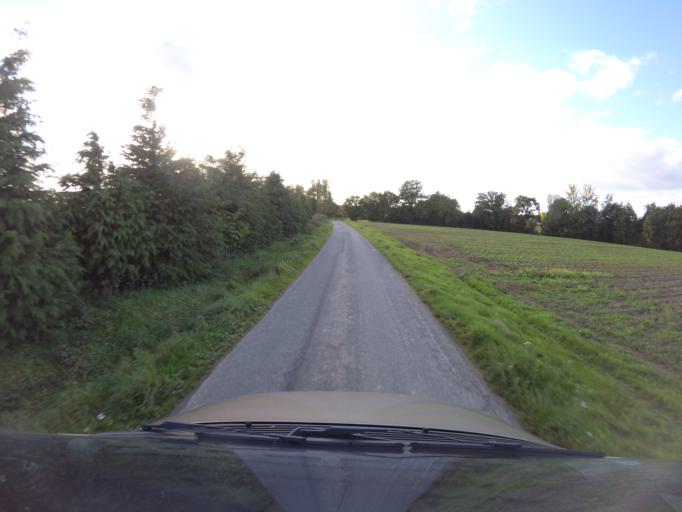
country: FR
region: Brittany
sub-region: Departement du Morbihan
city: Saint-Vincent-sur-Oust
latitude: 47.7143
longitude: -2.1703
